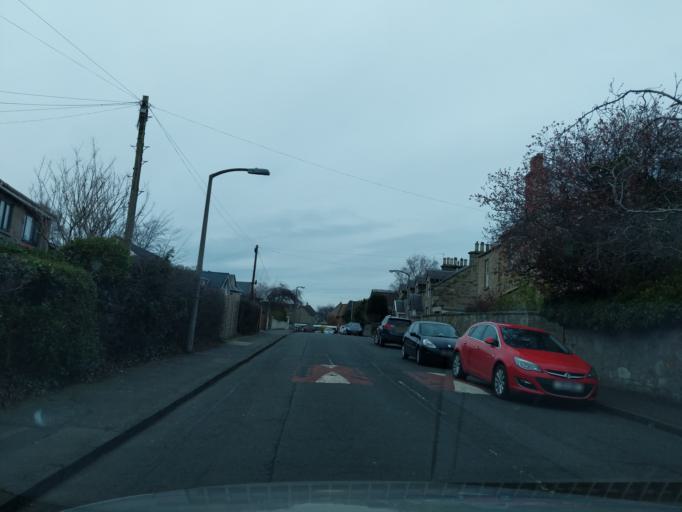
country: GB
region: Scotland
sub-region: Edinburgh
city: Colinton
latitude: 55.9388
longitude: -3.2865
